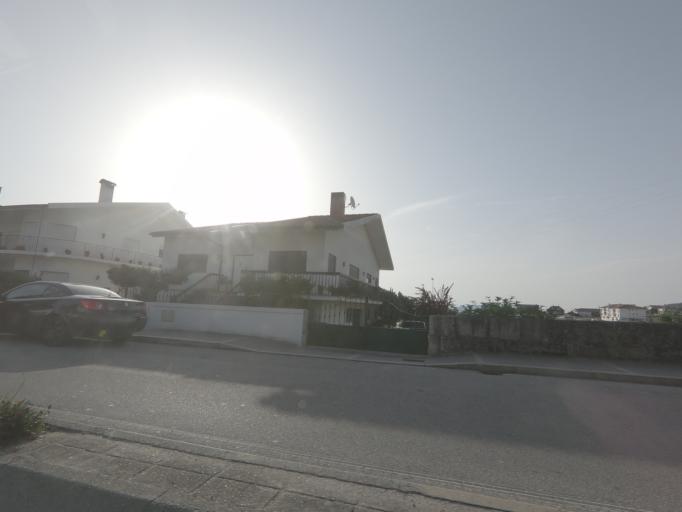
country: PT
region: Vila Real
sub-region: Sabrosa
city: Sabrosa
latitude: 41.2713
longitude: -7.4778
